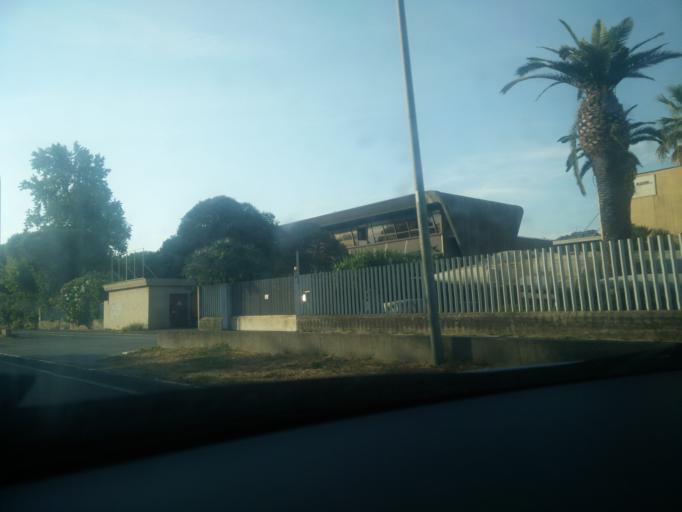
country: IT
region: Tuscany
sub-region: Provincia di Massa-Carrara
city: Massa
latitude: 44.0308
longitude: 10.0996
